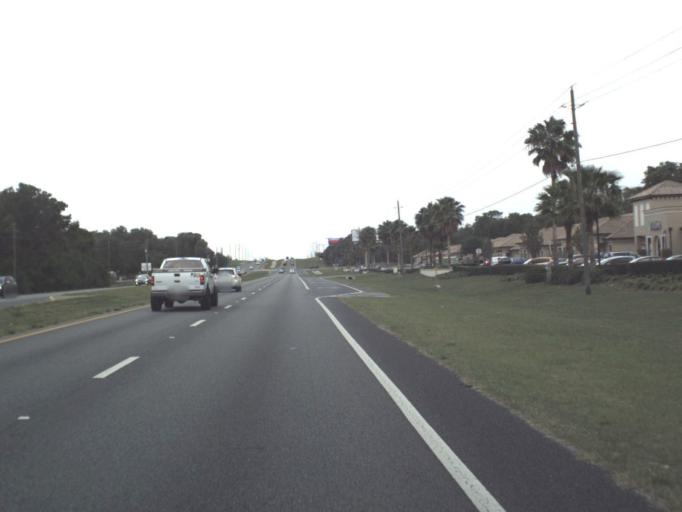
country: US
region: Florida
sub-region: Sumter County
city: The Villages
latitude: 28.9777
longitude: -81.9833
